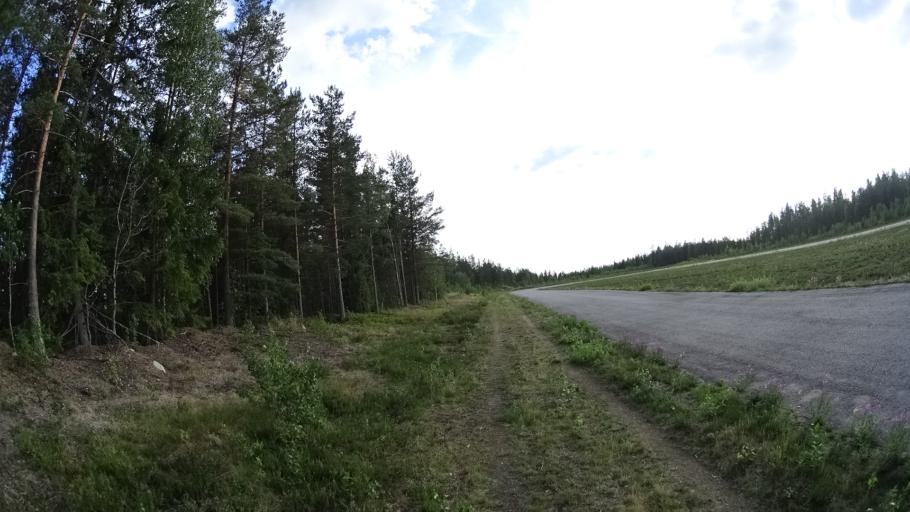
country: FI
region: Uusimaa
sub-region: Helsinki
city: Vihti
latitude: 60.3277
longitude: 24.2856
